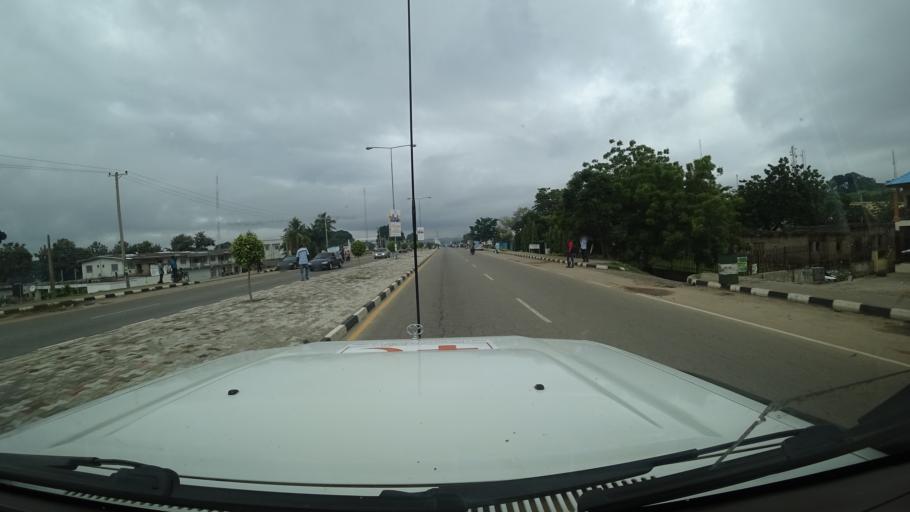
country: NG
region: Niger
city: Minna
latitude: 9.6053
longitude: 6.5559
